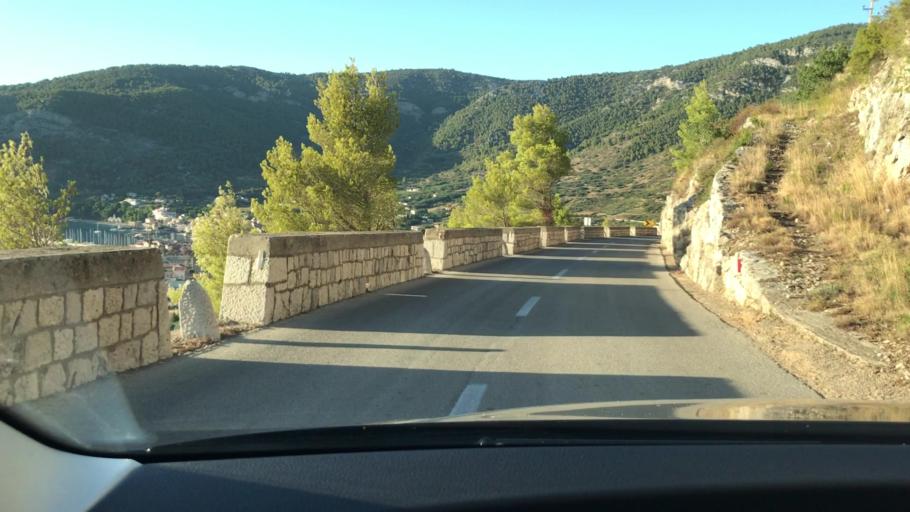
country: HR
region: Splitsko-Dalmatinska
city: Komiza
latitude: 43.0343
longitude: 16.0946
